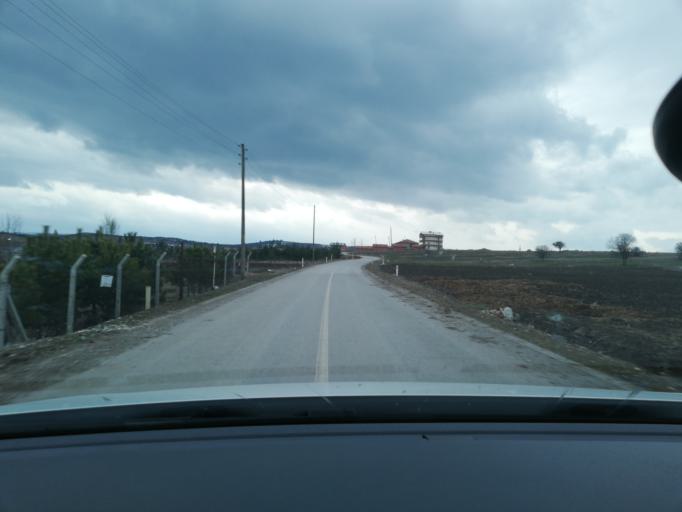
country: TR
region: Bolu
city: Gerede
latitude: 40.6936
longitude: 32.2176
